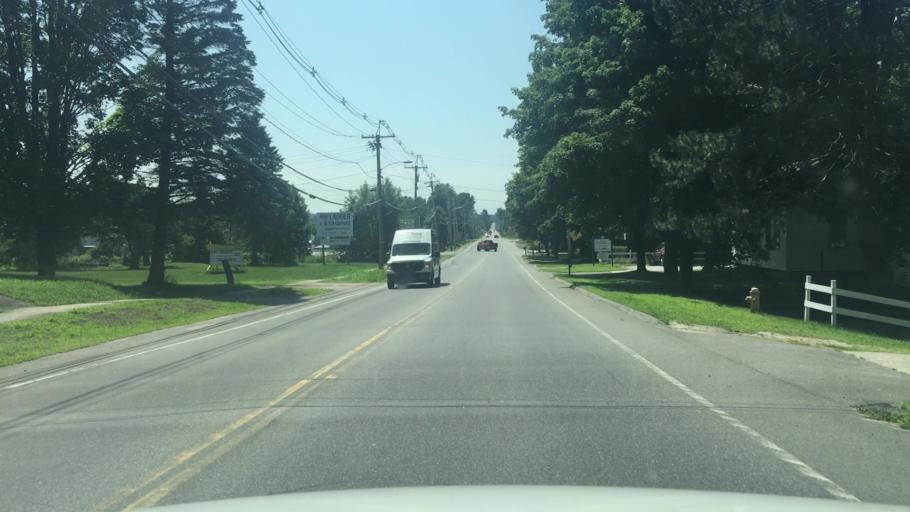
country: US
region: Maine
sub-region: Cumberland County
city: New Gloucester
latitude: 43.8833
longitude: -70.3301
